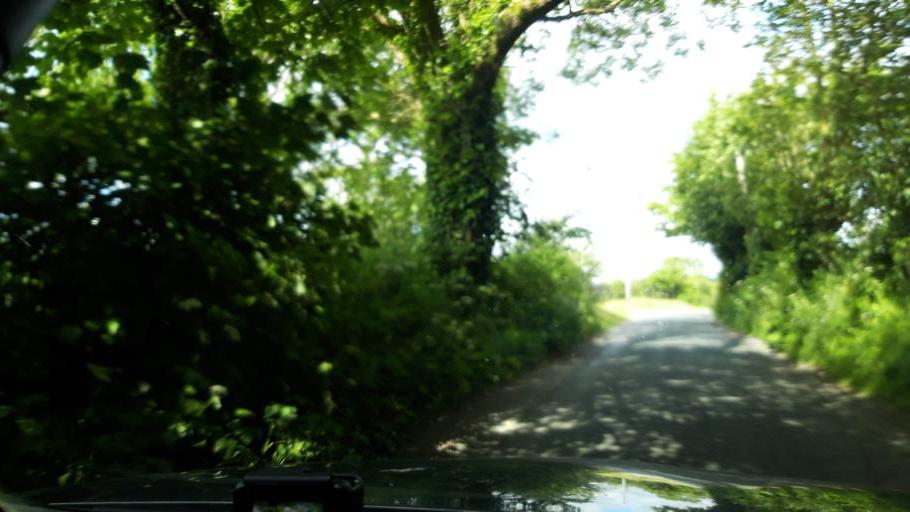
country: IE
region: Leinster
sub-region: Loch Garman
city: Loch Garman
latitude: 52.2850
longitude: -6.5065
